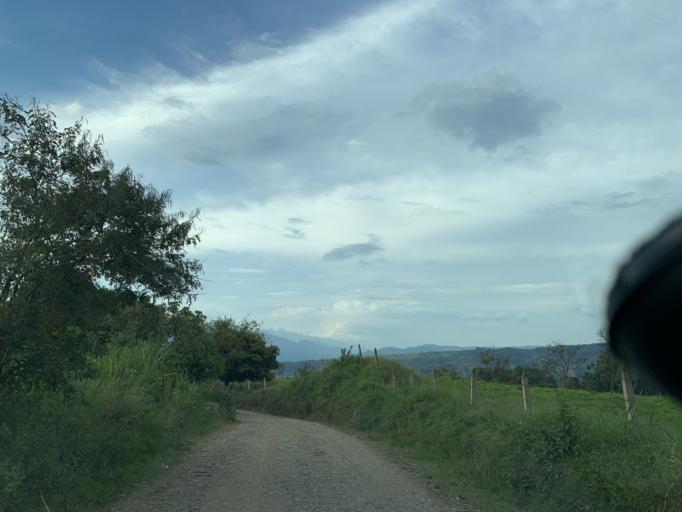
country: CO
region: Boyaca
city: Santana
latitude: 6.0720
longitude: -73.4855
